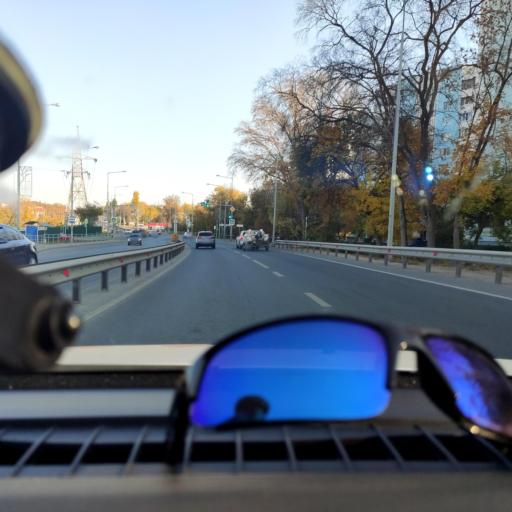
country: RU
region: Samara
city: Volzhskiy
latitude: 53.3519
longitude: 50.2142
